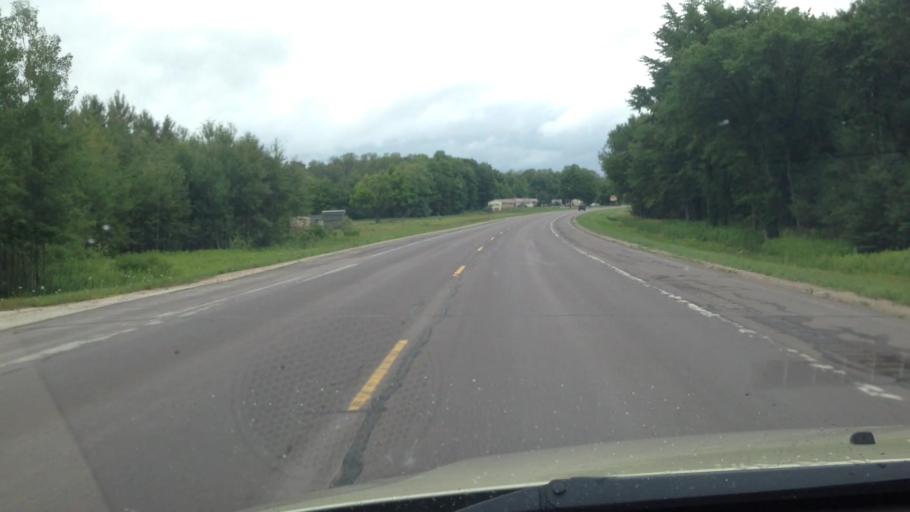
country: US
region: Michigan
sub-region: Schoolcraft County
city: Manistique
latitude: 46.0806
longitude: -85.9577
